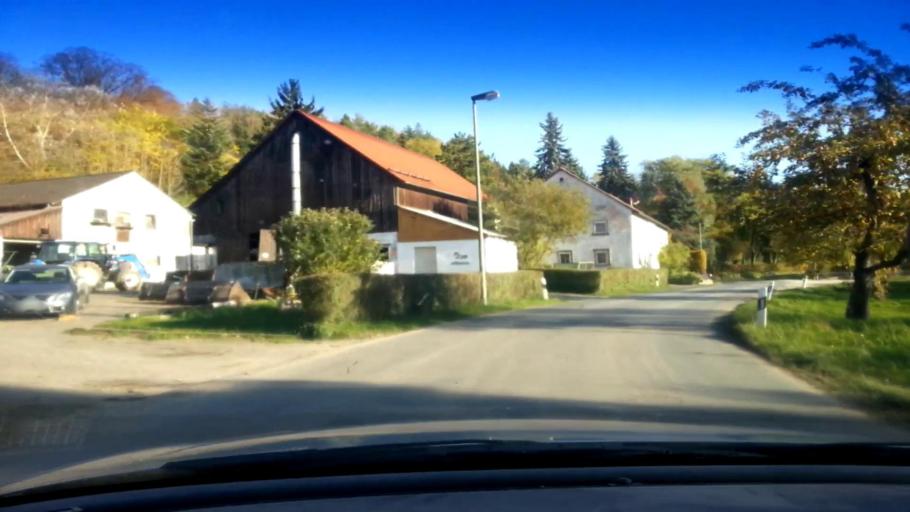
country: DE
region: Bavaria
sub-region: Upper Franconia
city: Heiligenstadt
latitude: 49.8820
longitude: 11.1311
